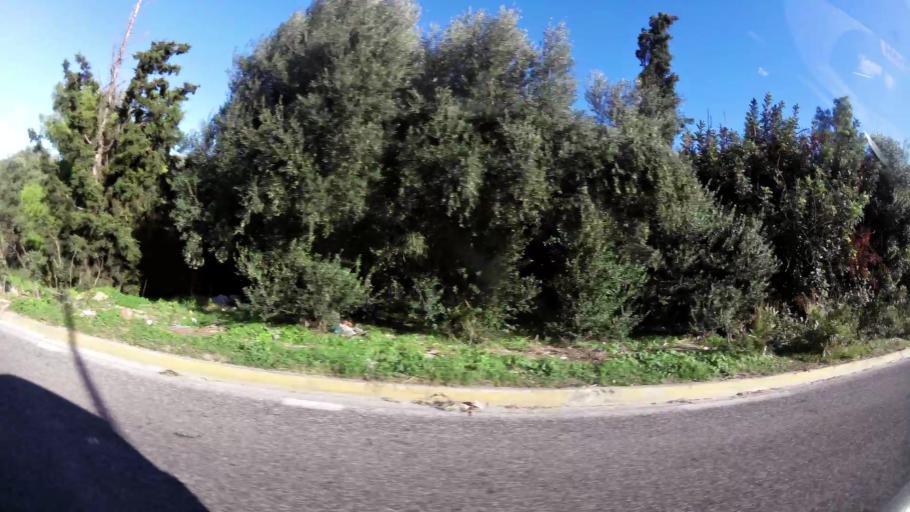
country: GR
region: Attica
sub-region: Nomarchia Athinas
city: Skaramangas
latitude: 38.0042
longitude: 23.6038
